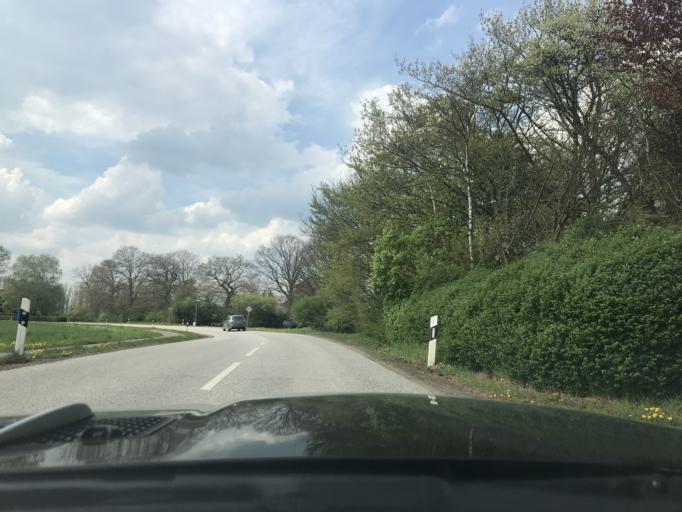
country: DE
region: Schleswig-Holstein
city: Schashagen
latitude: 54.1022
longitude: 10.8736
